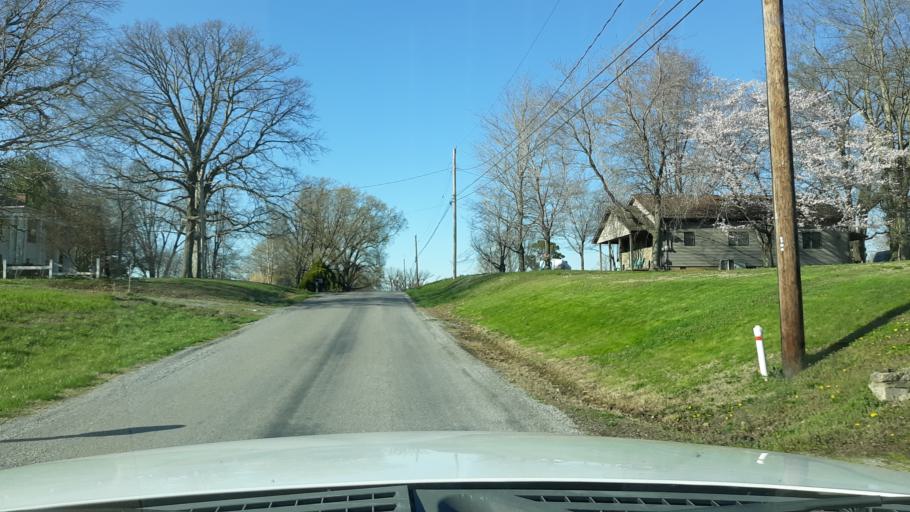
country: US
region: Illinois
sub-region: Saline County
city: Harrisburg
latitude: 37.7515
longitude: -88.5680
